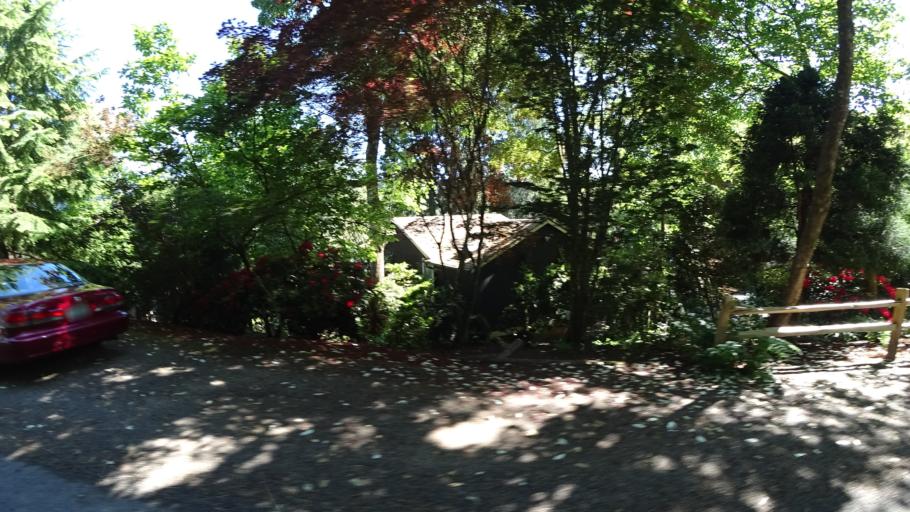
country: US
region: Oregon
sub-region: Washington County
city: Raleigh Hills
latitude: 45.4840
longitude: -122.7211
